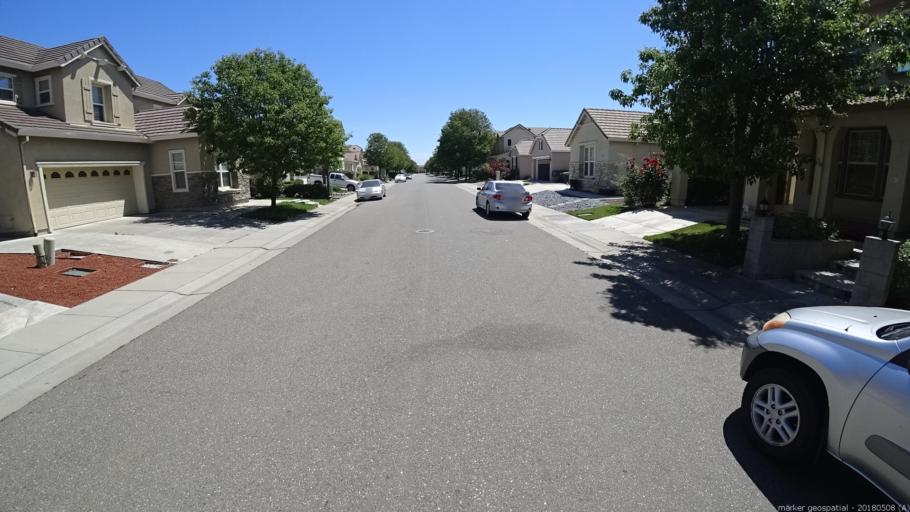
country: US
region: California
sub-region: Sacramento County
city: Elverta
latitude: 38.6819
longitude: -121.5381
